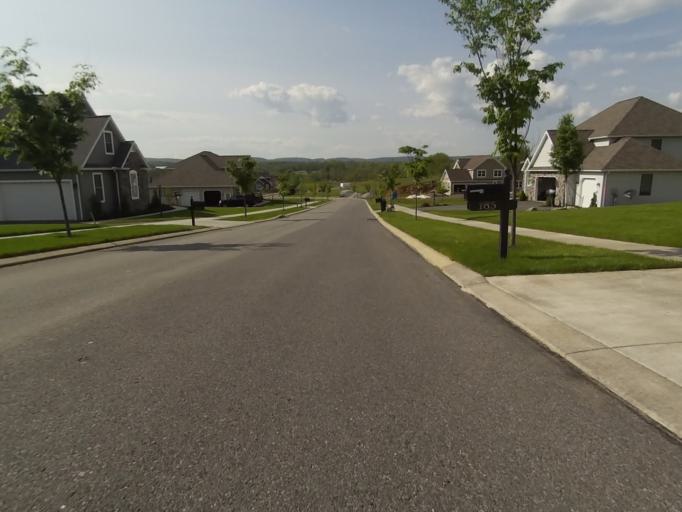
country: US
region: Pennsylvania
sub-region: Centre County
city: Houserville
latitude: 40.8283
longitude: -77.8209
